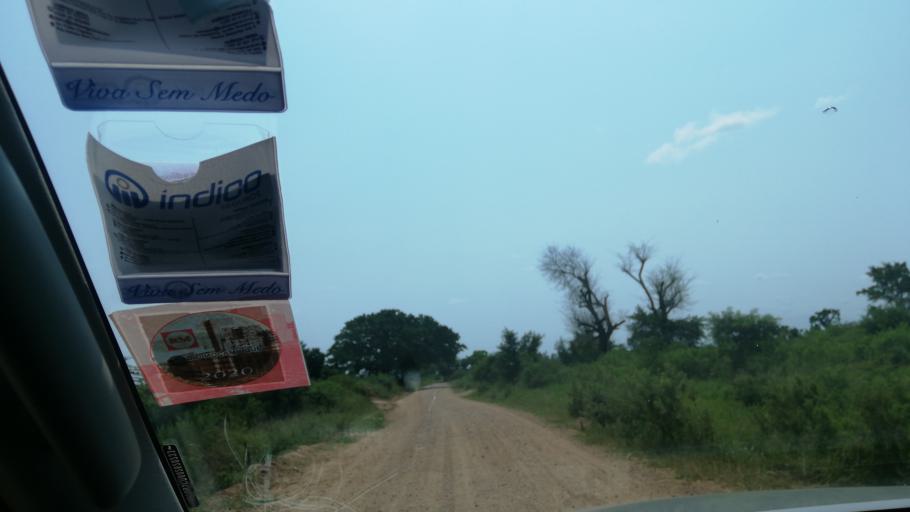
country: MZ
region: Maputo
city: Matola
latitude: -26.0590
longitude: 32.3897
